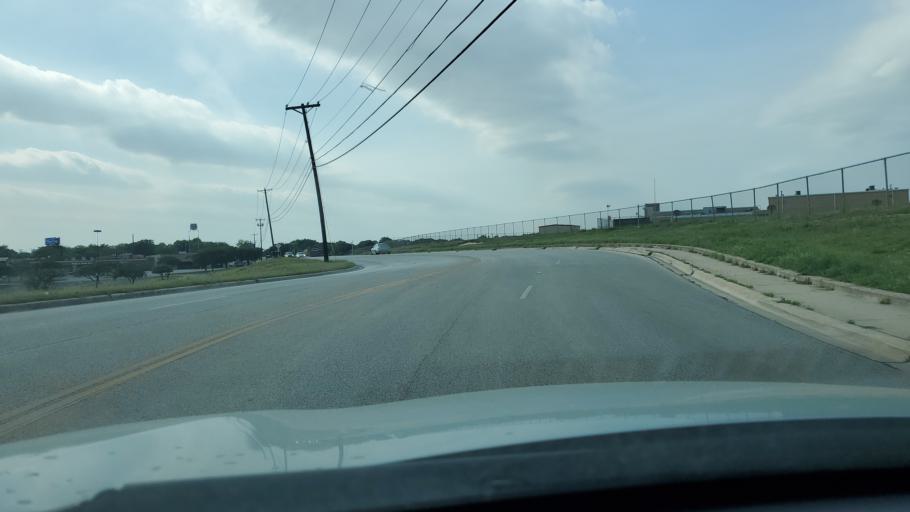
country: US
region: Texas
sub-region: Bell County
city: Killeen
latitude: 31.0948
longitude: -97.7172
